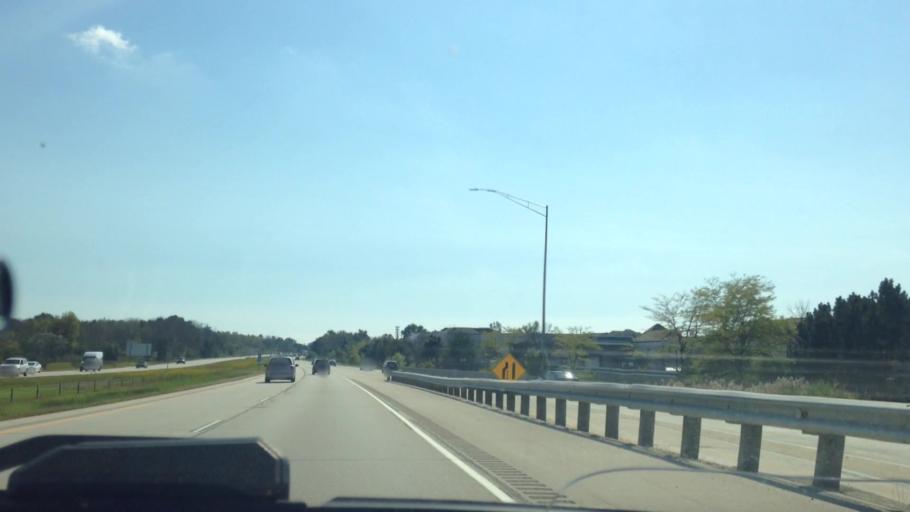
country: US
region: Wisconsin
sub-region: Milwaukee County
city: Bayside
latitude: 43.2196
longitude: -87.9217
